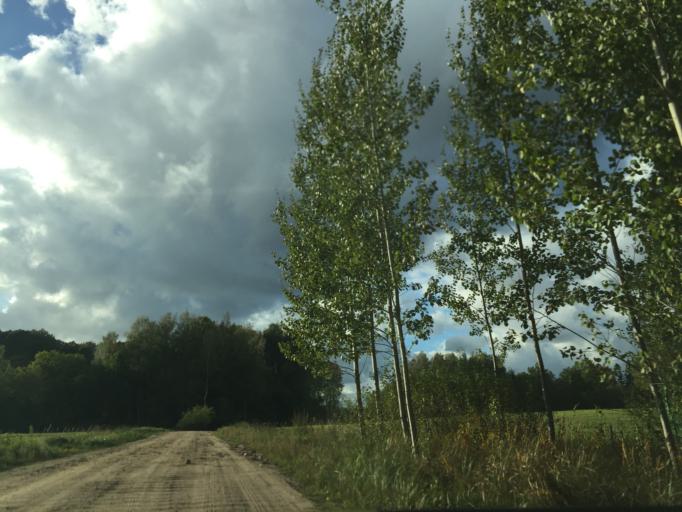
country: LV
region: Ligatne
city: Ligatne
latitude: 57.1378
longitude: 25.0857
